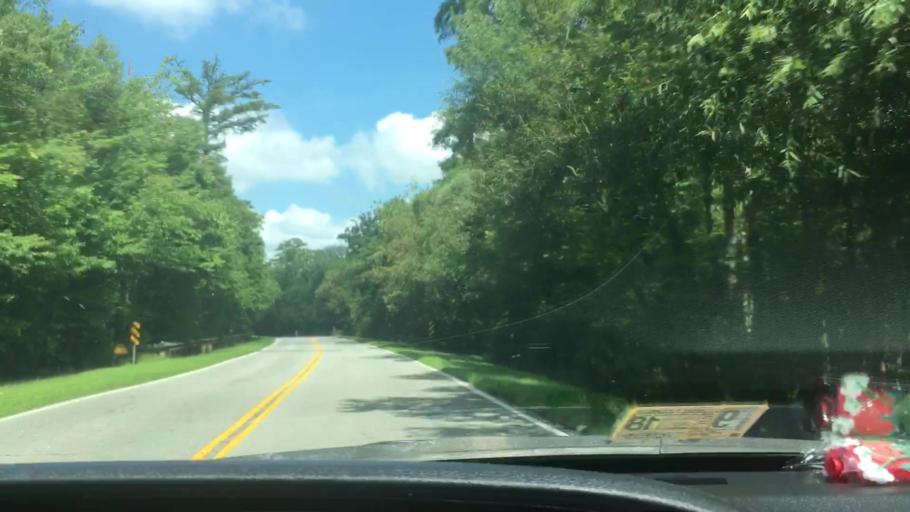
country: US
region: Virginia
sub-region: City of Virginia Beach
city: Virginia Beach
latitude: 36.7438
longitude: -76.1153
